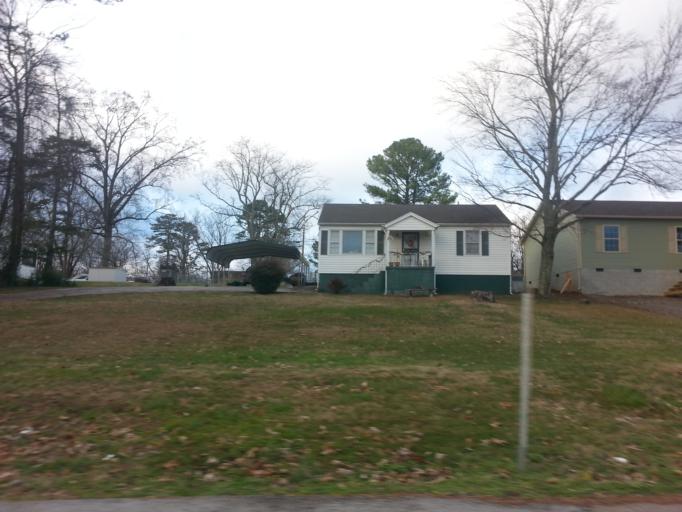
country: US
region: Tennessee
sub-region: Knox County
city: Knoxville
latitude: 35.9985
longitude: -83.9031
